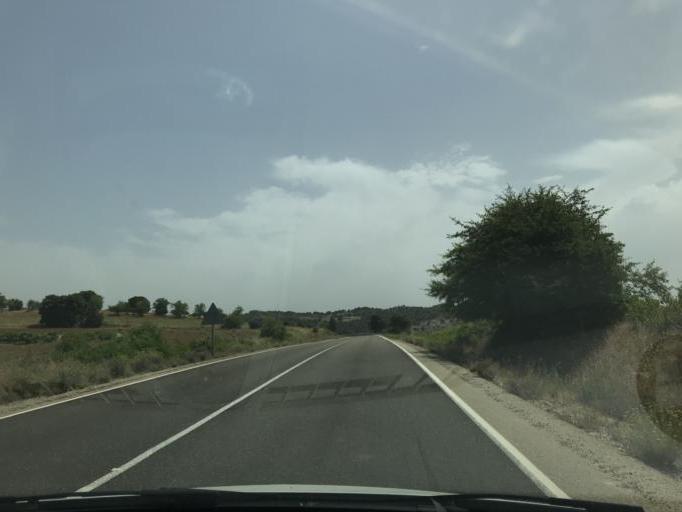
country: ES
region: Castille-La Mancha
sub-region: Provincia de Cuenca
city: Albalate de las Nogueras
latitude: 40.3944
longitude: -2.2602
